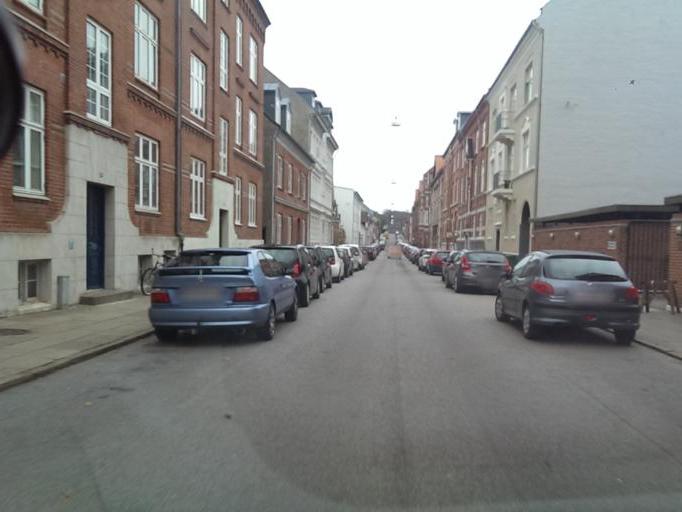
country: DK
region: South Denmark
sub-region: Esbjerg Kommune
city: Esbjerg
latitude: 55.4688
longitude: 8.4418
